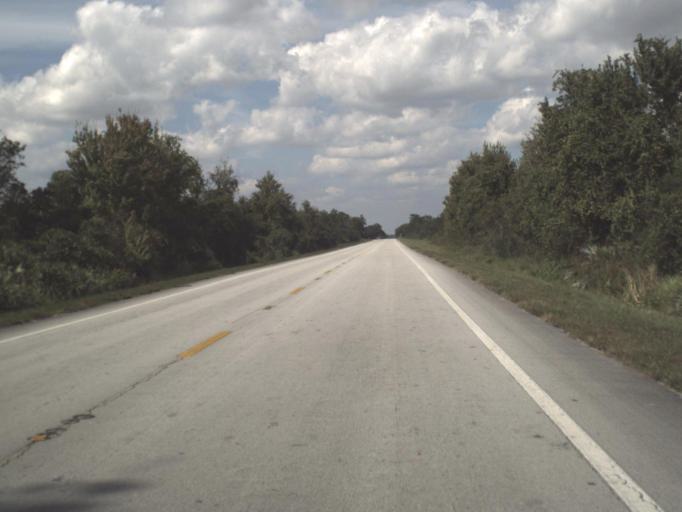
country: US
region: Florida
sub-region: Okeechobee County
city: Cypress Quarters
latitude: 27.5372
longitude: -80.8103
